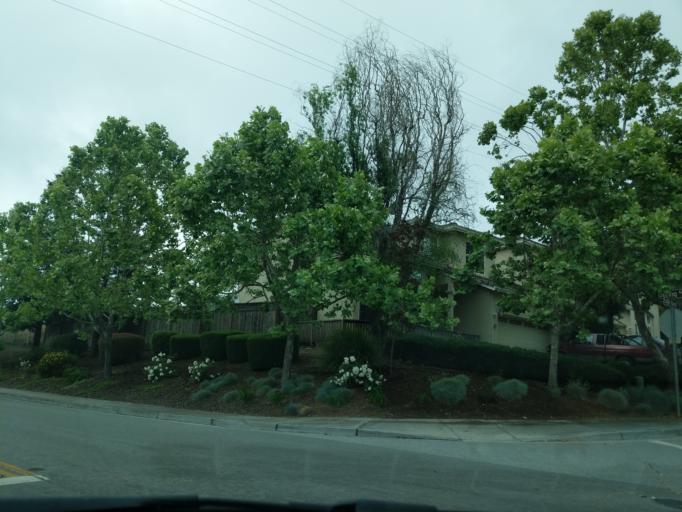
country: US
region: California
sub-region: Santa Clara County
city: Morgan Hill
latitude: 37.1189
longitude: -121.6568
